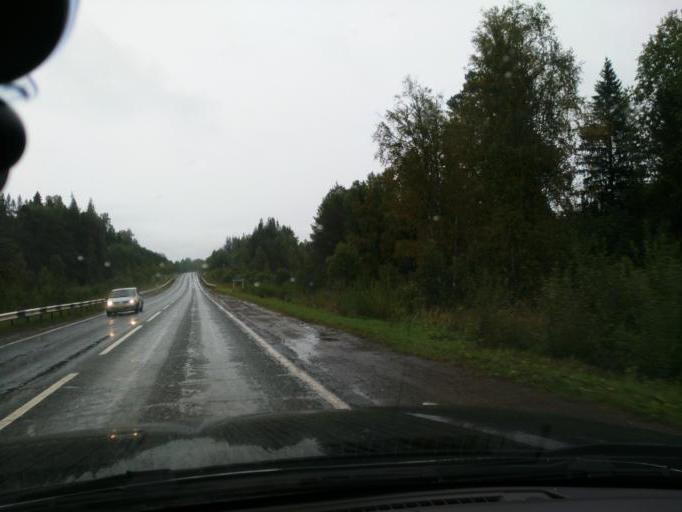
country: RU
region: Perm
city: Yugo-Kamskiy
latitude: 57.6543
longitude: 55.5974
